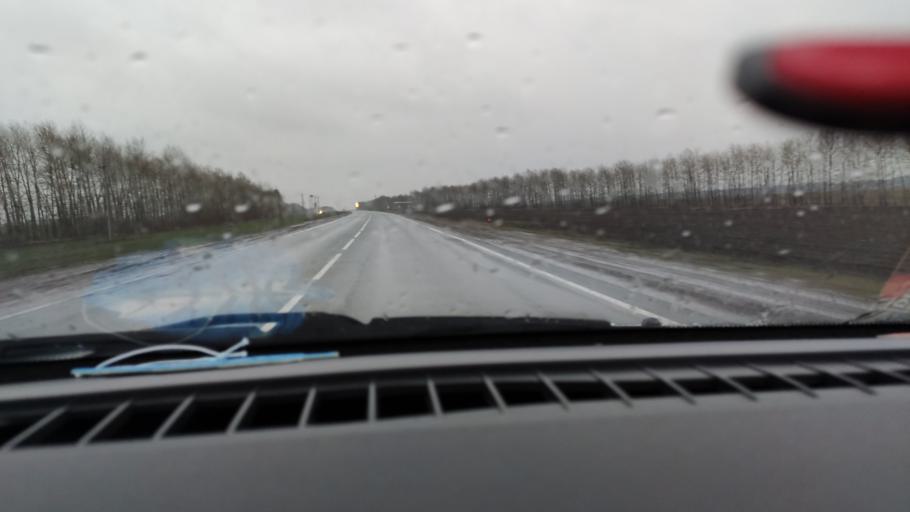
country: RU
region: Tatarstan
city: Mendeleyevsk
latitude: 55.9197
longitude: 52.2740
